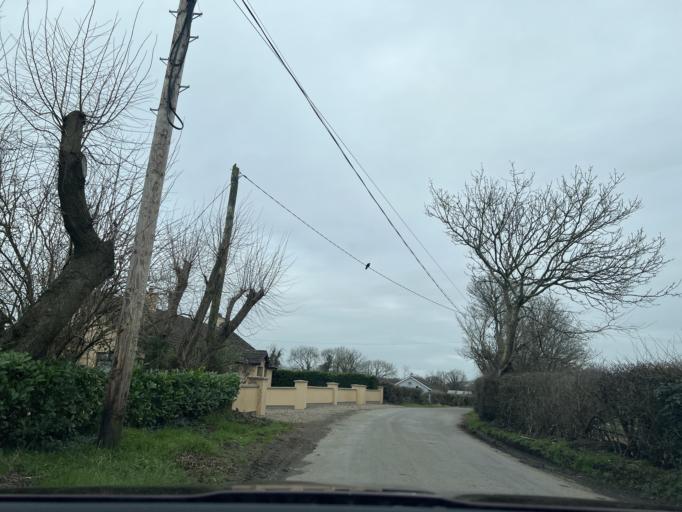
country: IE
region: Leinster
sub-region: Loch Garman
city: Castlebridge
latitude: 52.3788
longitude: -6.5252
